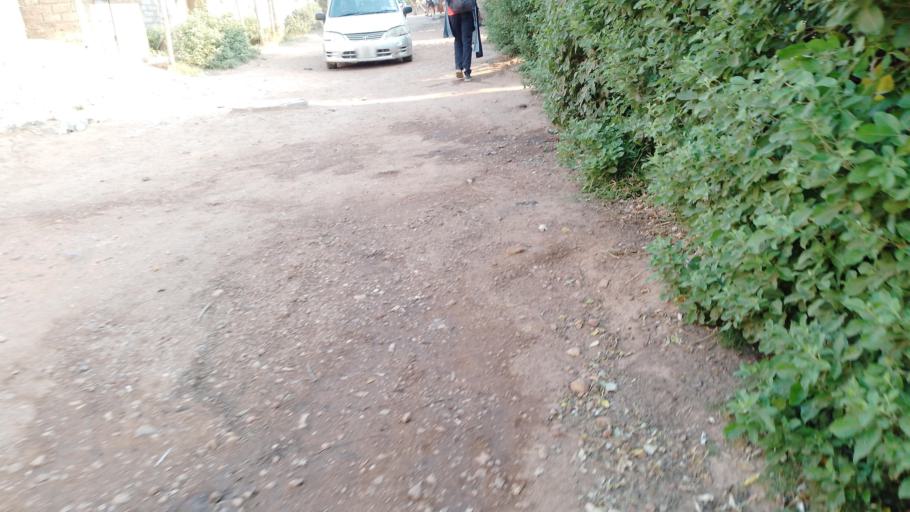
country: ZM
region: Lusaka
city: Lusaka
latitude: -15.3995
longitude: 28.3697
